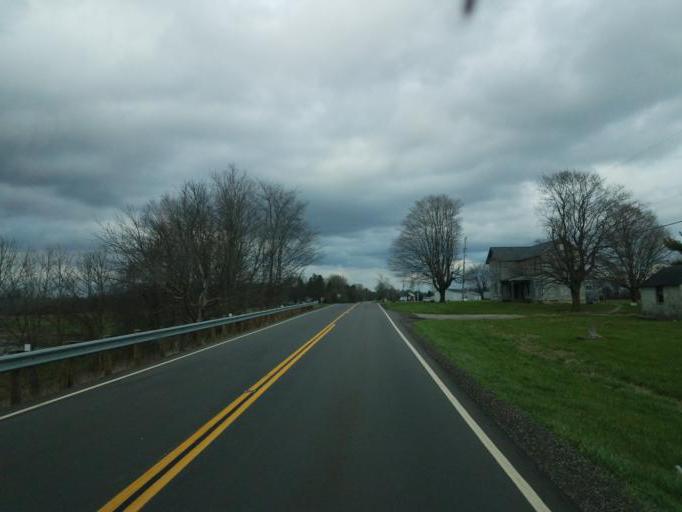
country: US
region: Ohio
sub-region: Morrow County
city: Cardington
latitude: 40.4920
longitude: -82.9229
